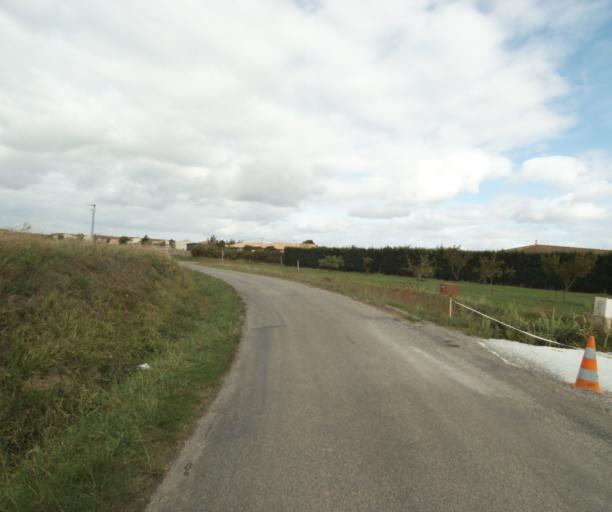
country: FR
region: Midi-Pyrenees
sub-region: Departement du Tarn-et-Garonne
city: Finhan
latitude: 43.8966
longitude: 1.1247
